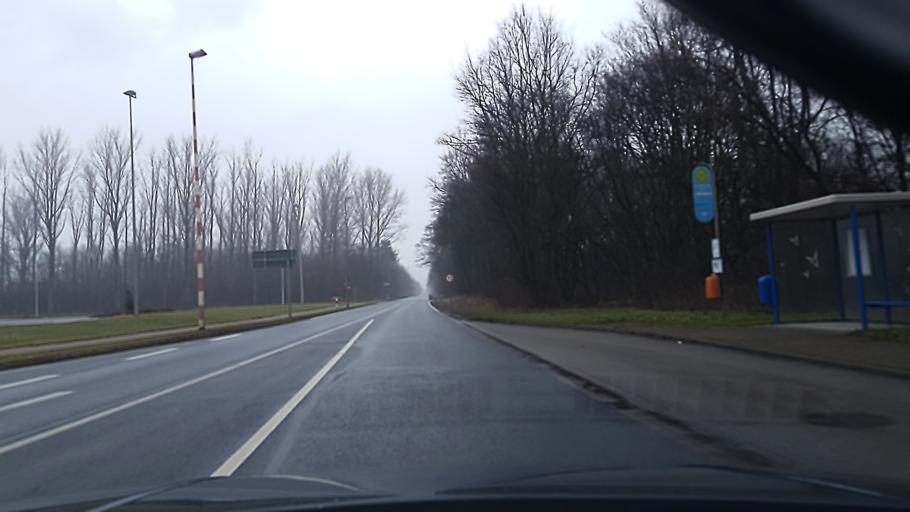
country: DE
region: Lower Saxony
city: Cramme
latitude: 52.1564
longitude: 10.4240
